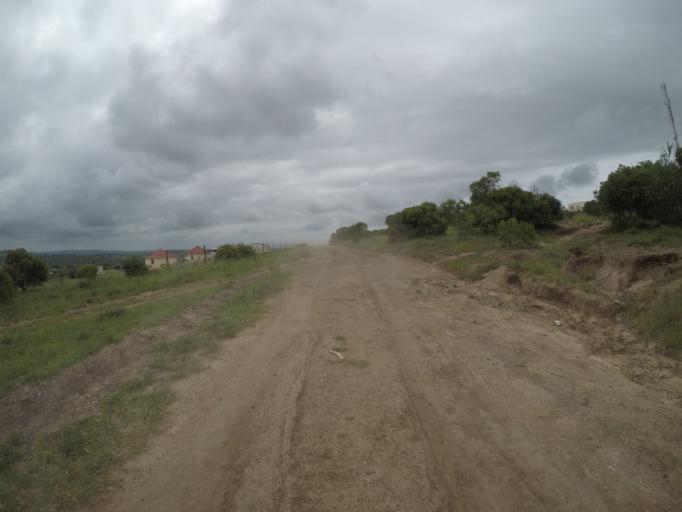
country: ZA
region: KwaZulu-Natal
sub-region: uThungulu District Municipality
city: Empangeni
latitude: -28.6038
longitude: 31.8338
